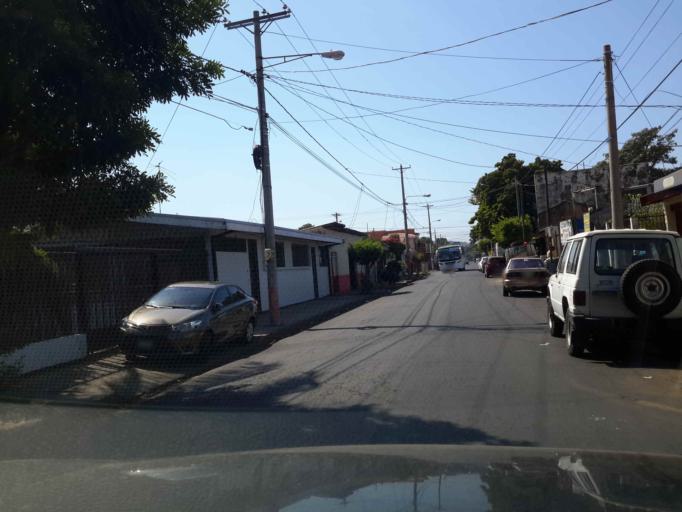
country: NI
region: Managua
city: Managua
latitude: 12.1479
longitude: -86.2902
